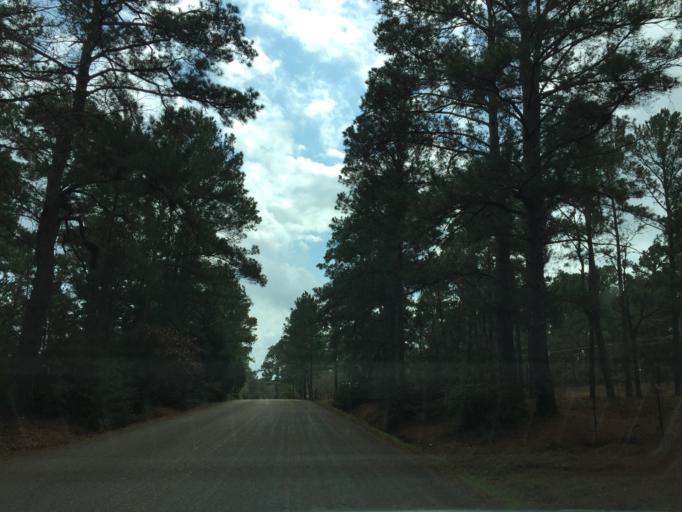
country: US
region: Texas
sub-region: Bastrop County
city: Bastrop
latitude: 30.1249
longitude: -97.2797
